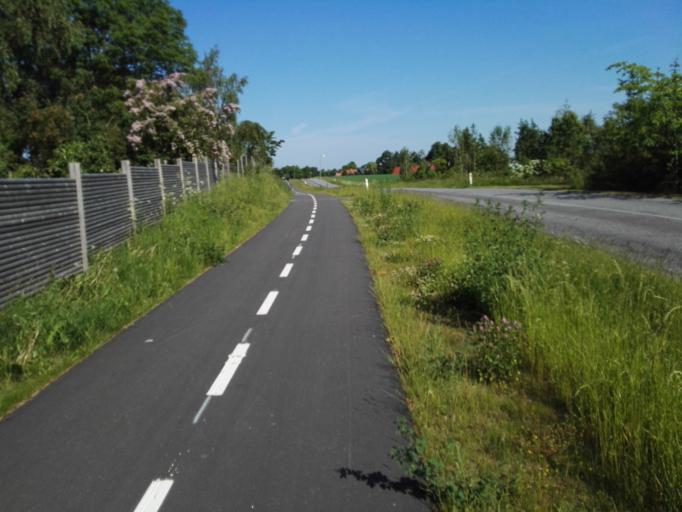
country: DK
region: Zealand
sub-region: Lejre Kommune
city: Ejby
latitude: 55.7145
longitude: 11.8929
